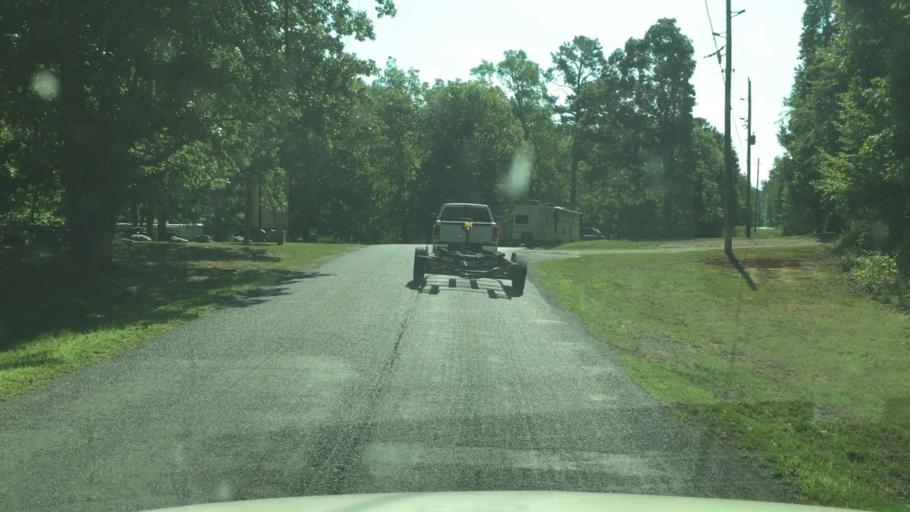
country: US
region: Arkansas
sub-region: Garland County
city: Piney
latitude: 34.5417
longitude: -93.3520
